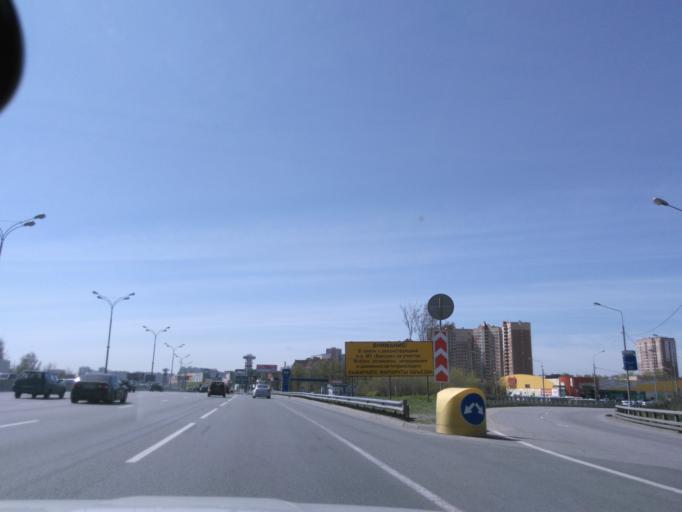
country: RU
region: Moscow
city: Khimki
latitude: 55.8655
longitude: 37.4029
